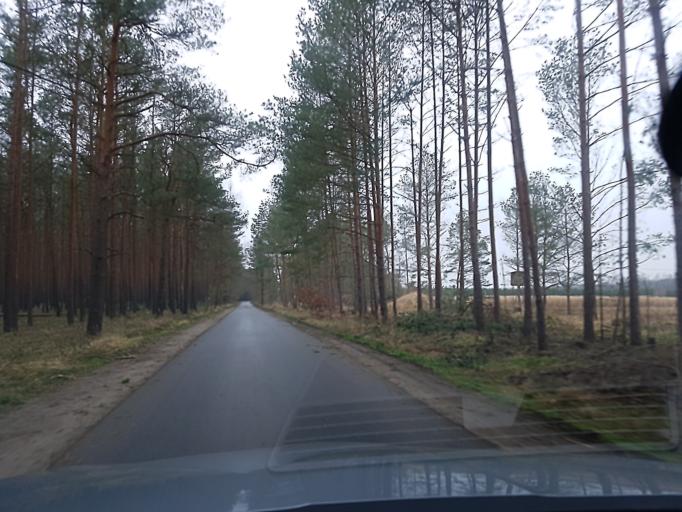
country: DE
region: Brandenburg
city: Schonewalde
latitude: 51.6547
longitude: 13.6267
